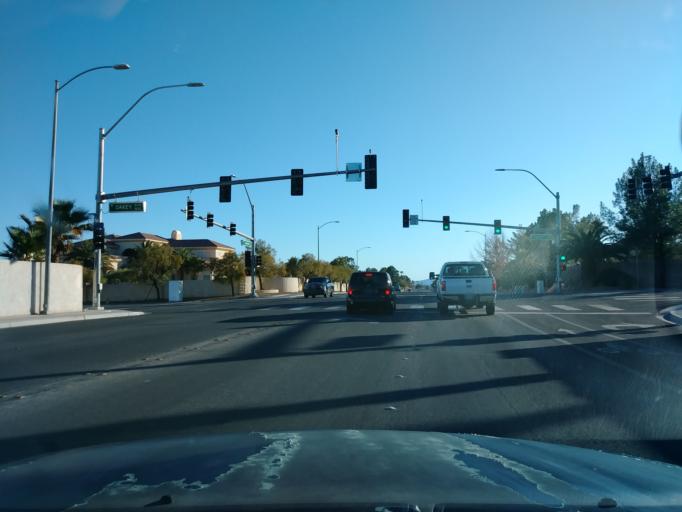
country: US
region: Nevada
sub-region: Clark County
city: Spring Valley
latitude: 36.1517
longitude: -115.2707
